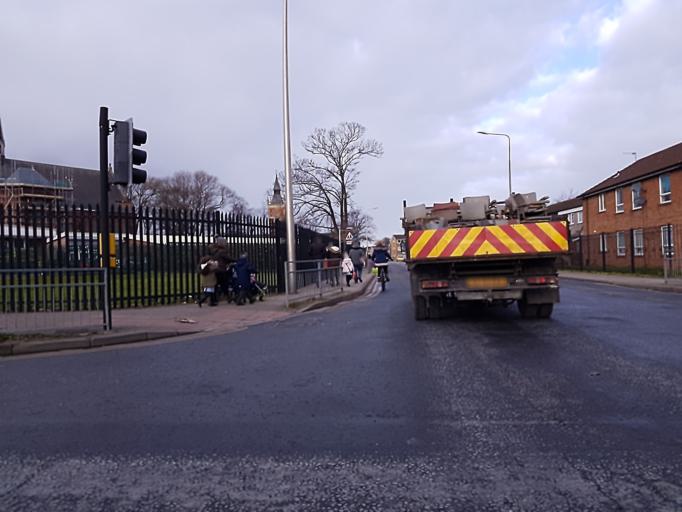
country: GB
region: England
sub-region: North East Lincolnshire
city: Grimsby
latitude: 53.5680
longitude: -0.0690
